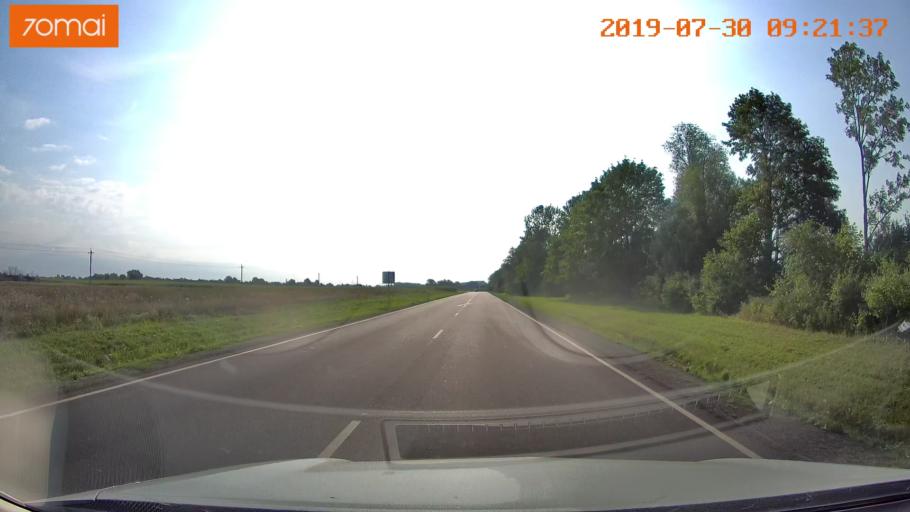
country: RU
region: Kaliningrad
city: Nesterov
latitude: 54.6351
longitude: 22.6355
